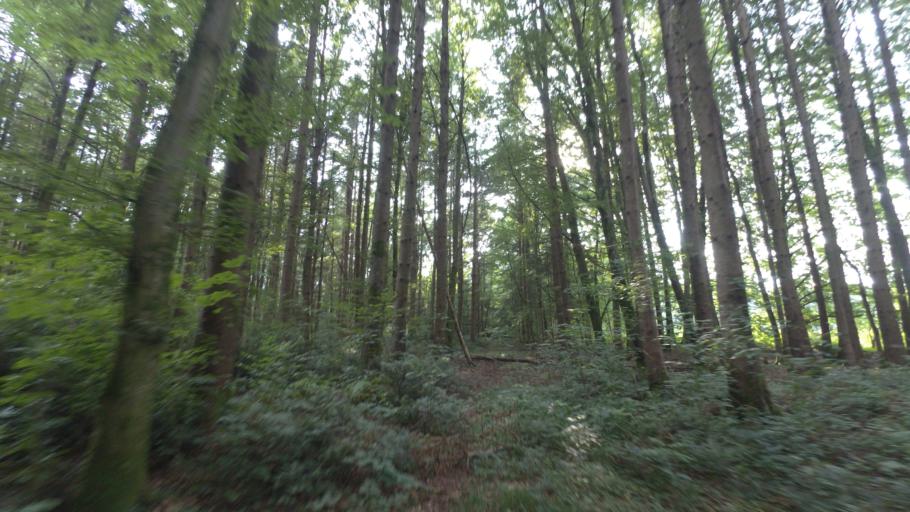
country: DE
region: Bavaria
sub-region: Upper Bavaria
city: Nussdorf
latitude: 47.9293
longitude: 12.5627
